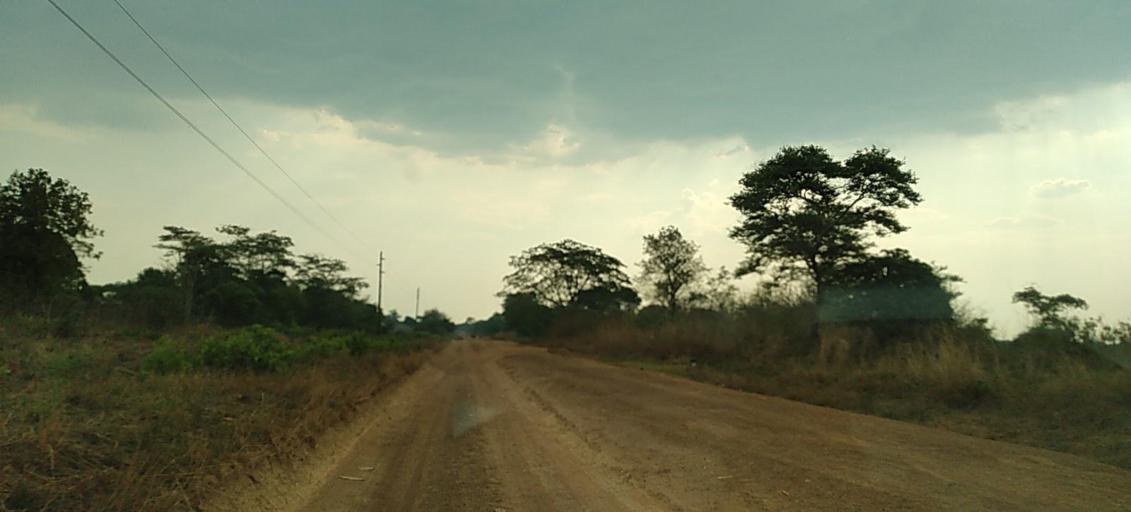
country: ZM
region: Copperbelt
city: Kalulushi
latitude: -12.9507
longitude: 27.9102
